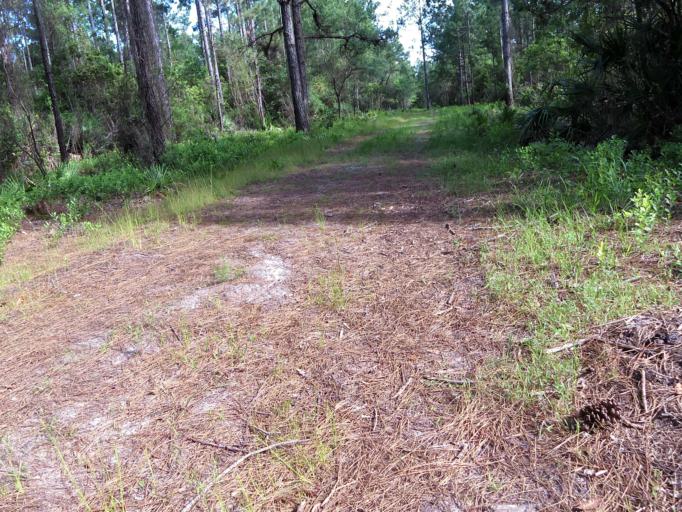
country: US
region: Florida
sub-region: Duval County
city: Atlantic Beach
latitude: 30.4470
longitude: -81.4707
